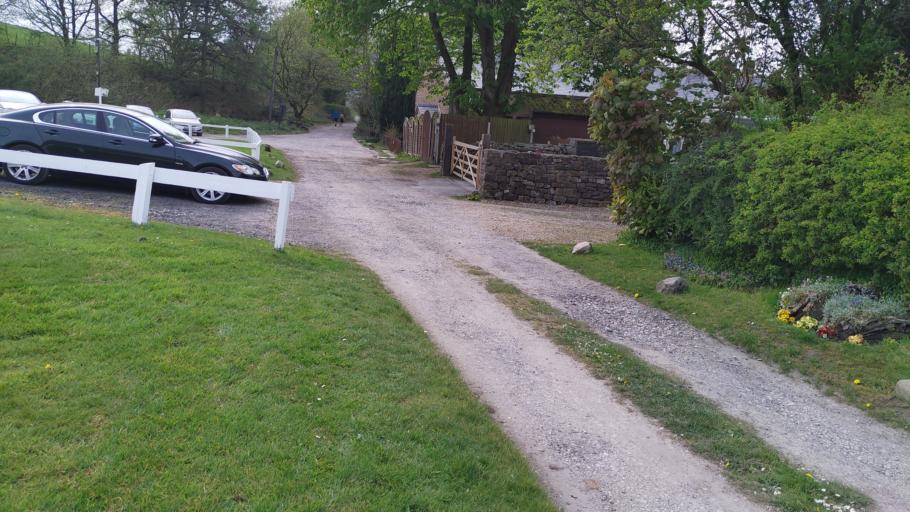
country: GB
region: England
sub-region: Lancashire
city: Chorley
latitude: 53.6671
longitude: -2.5775
